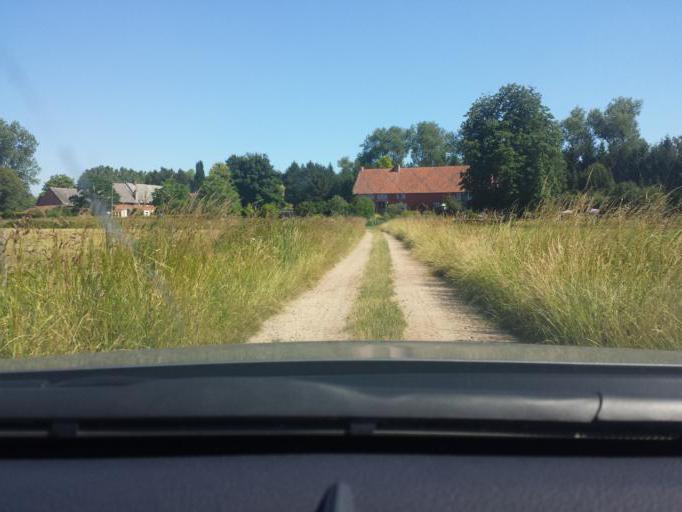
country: BE
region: Flanders
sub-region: Provincie Limburg
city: Lummen
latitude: 50.9714
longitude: 5.1818
